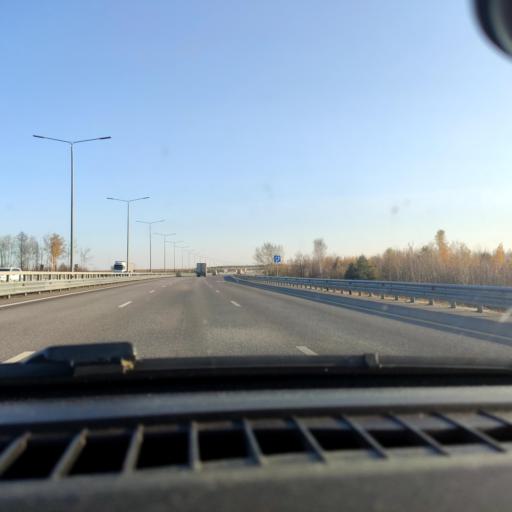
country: RU
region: Voronezj
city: Somovo
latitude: 51.7799
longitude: 39.2950
